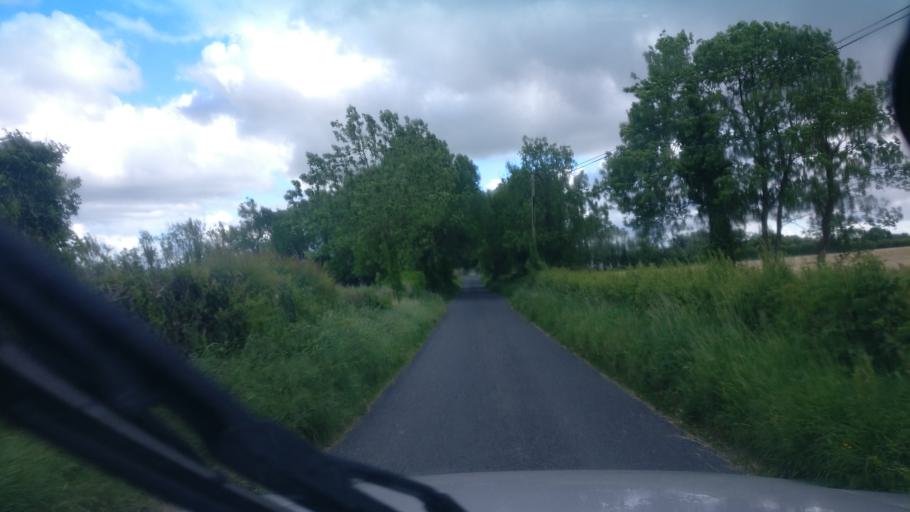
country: IE
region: Connaught
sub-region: County Galway
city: Portumna
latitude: 53.1829
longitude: -8.3394
